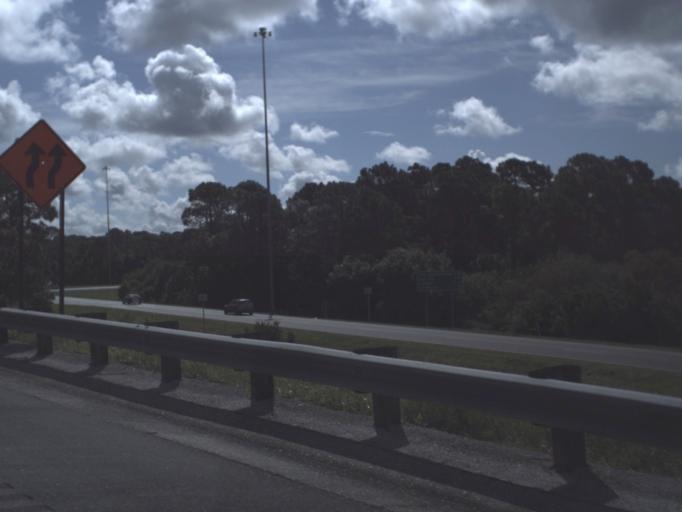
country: US
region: Florida
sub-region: Sarasota County
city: Plantation
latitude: 27.1098
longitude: -82.3503
